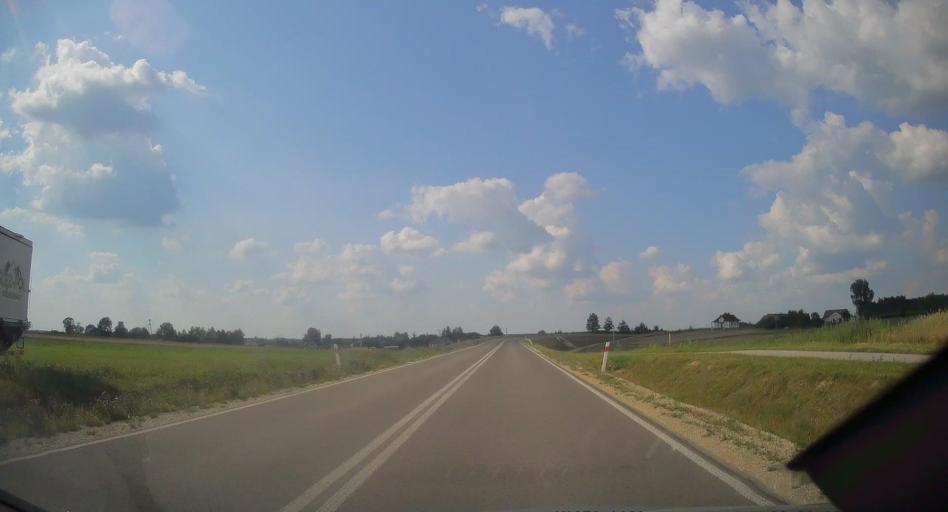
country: PL
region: Swietokrzyskie
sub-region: Powiat kielecki
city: Lopuszno
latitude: 50.9738
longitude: 20.2483
